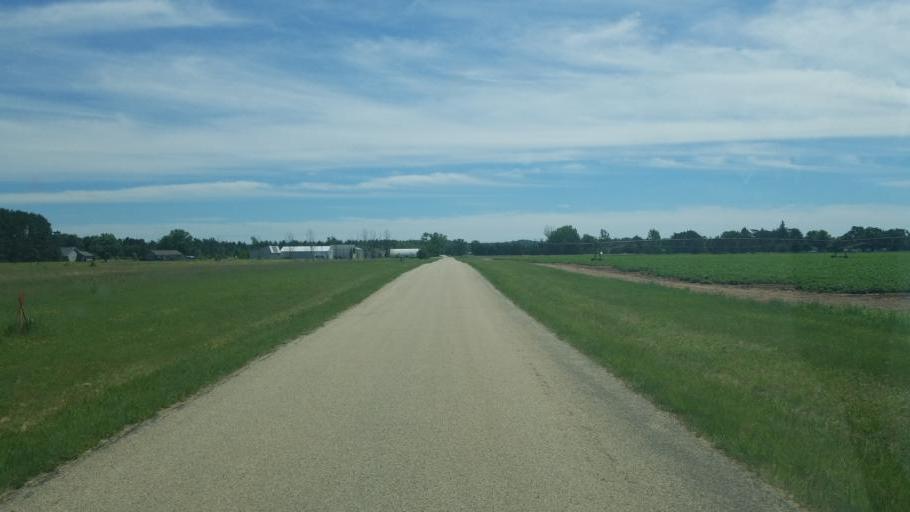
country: US
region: Wisconsin
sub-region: Adams County
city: Adams
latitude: 43.8764
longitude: -89.9445
